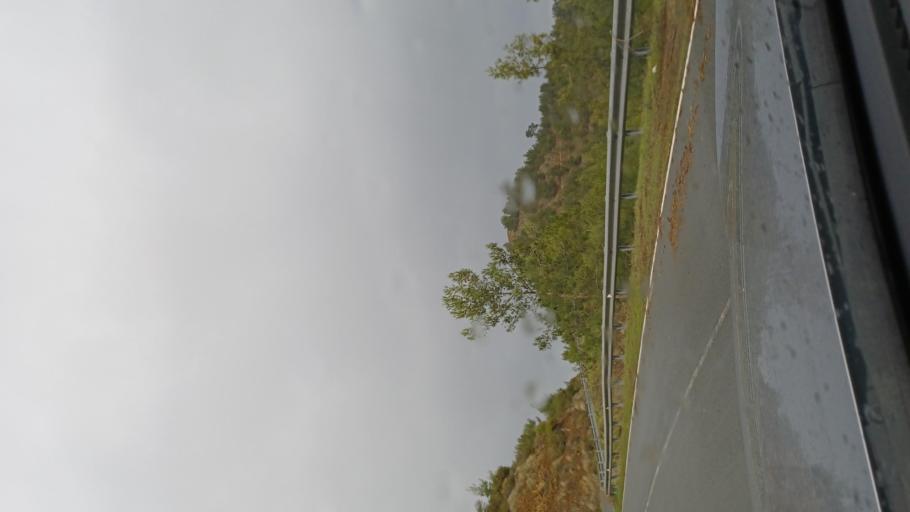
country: CY
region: Lefkosia
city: Kato Pyrgos
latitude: 35.1132
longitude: 32.7277
